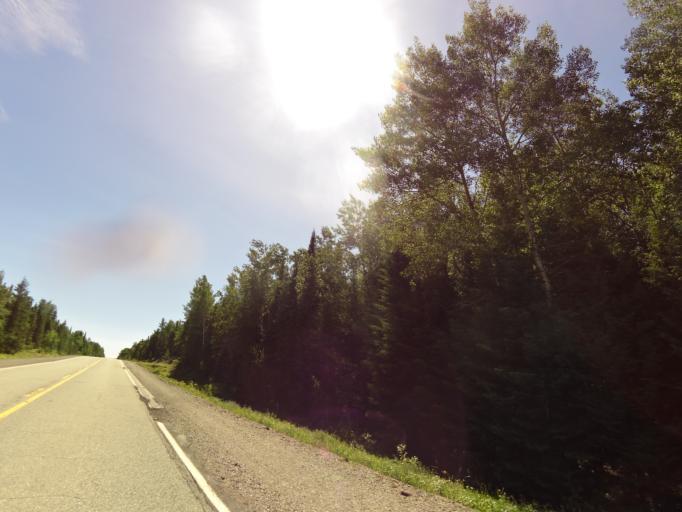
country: CA
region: Quebec
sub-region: Nord-du-Quebec
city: Lebel-sur-Quevillon
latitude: 48.8259
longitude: -77.1199
